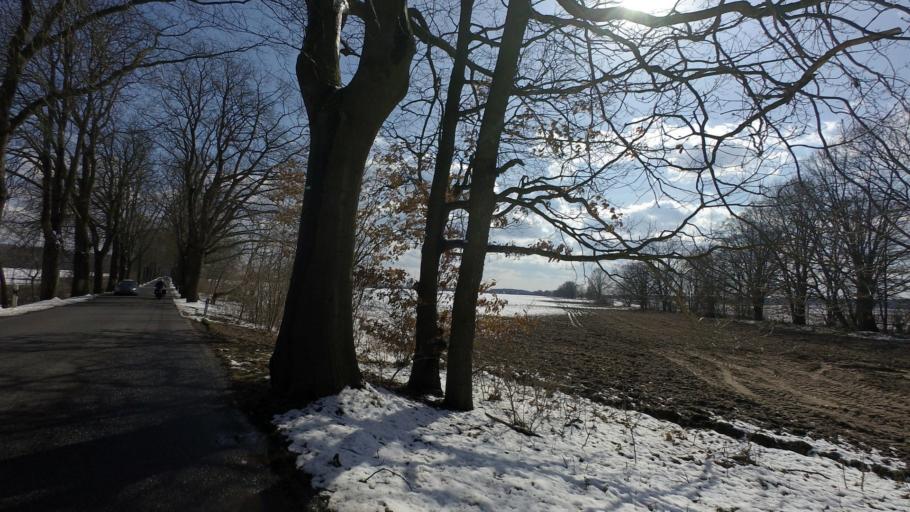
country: DE
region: Brandenburg
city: Joachimsthal
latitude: 52.9028
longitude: 13.7111
